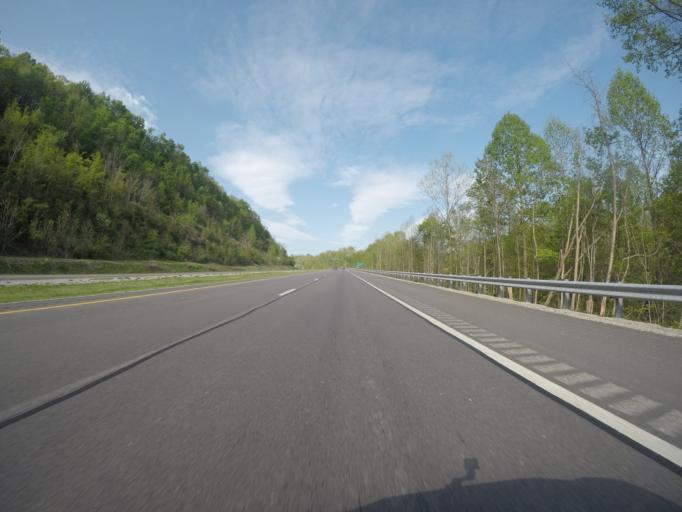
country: US
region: West Virginia
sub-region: Kanawha County
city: Dunbar
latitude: 38.2995
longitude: -81.7430
